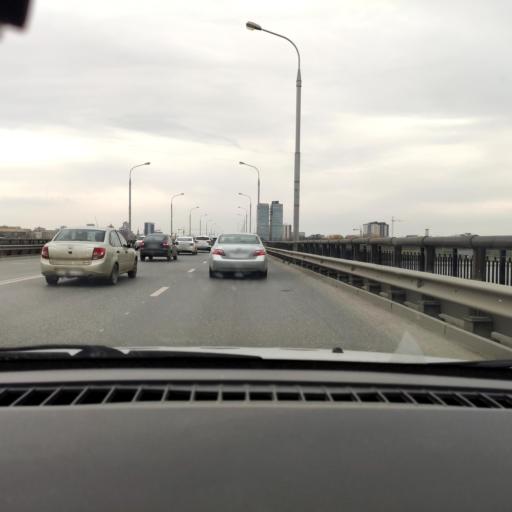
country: RU
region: Perm
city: Perm
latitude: 58.0239
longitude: 56.2192
